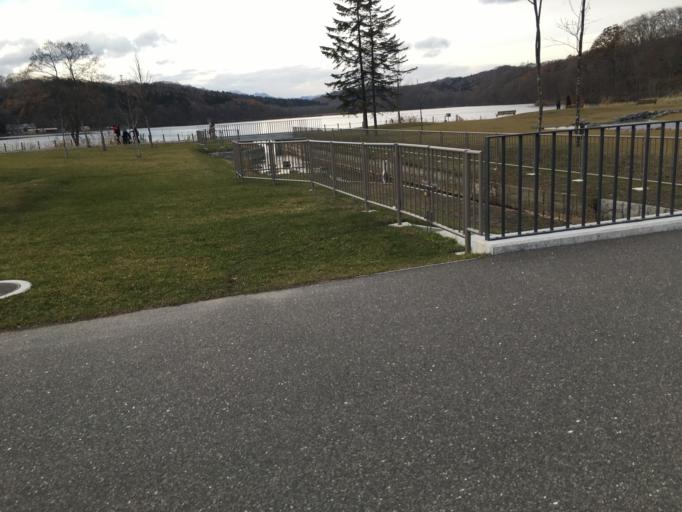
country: JP
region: Hokkaido
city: Shiraoi
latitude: 42.5606
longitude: 141.3665
